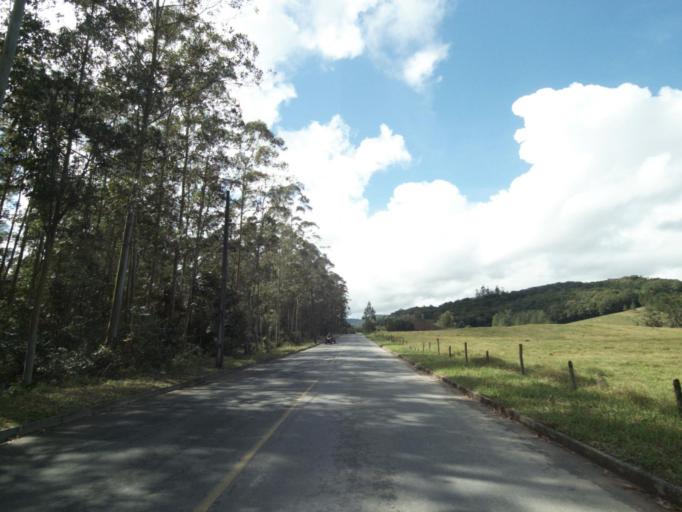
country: BR
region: Santa Catarina
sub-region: Pomerode
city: Pomerode
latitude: -26.6879
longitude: -49.1741
